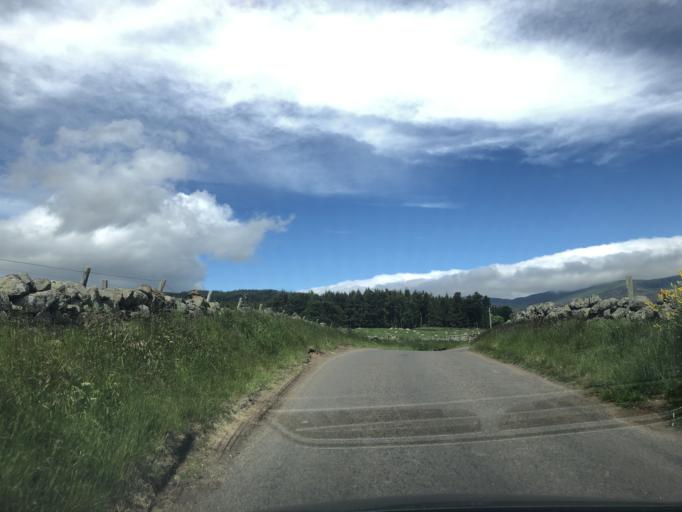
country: GB
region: Scotland
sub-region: Angus
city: Kirriemuir
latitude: 56.8060
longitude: -3.0492
